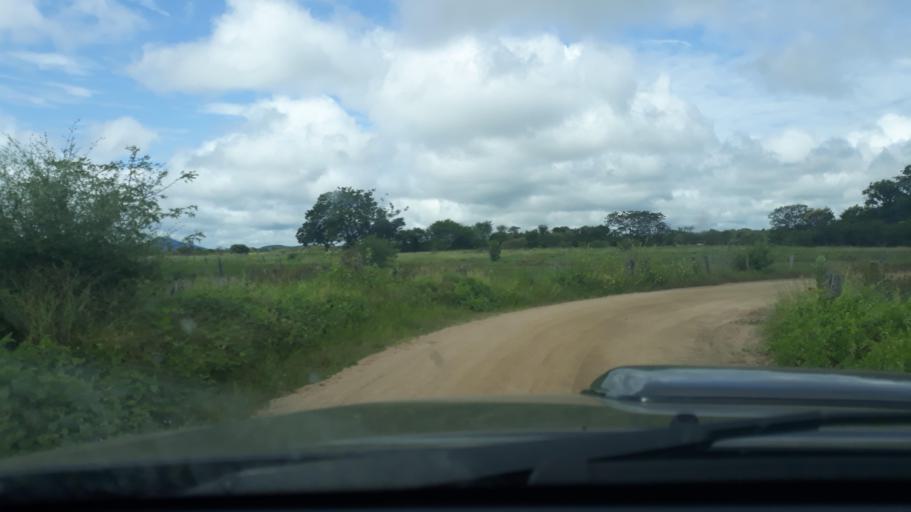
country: BR
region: Bahia
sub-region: Riacho De Santana
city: Riacho de Santana
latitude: -13.9114
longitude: -42.9473
